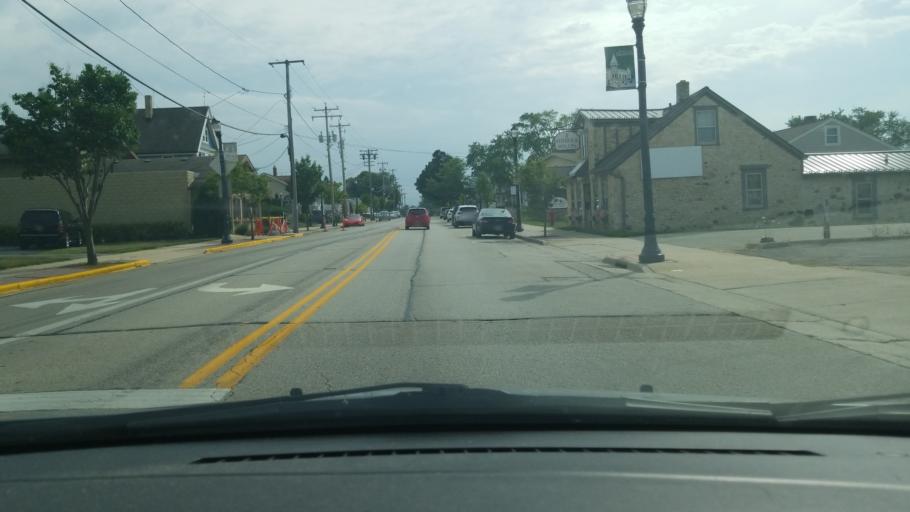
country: US
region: Wisconsin
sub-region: Ozaukee County
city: Grafton
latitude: 43.3164
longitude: -87.9533
